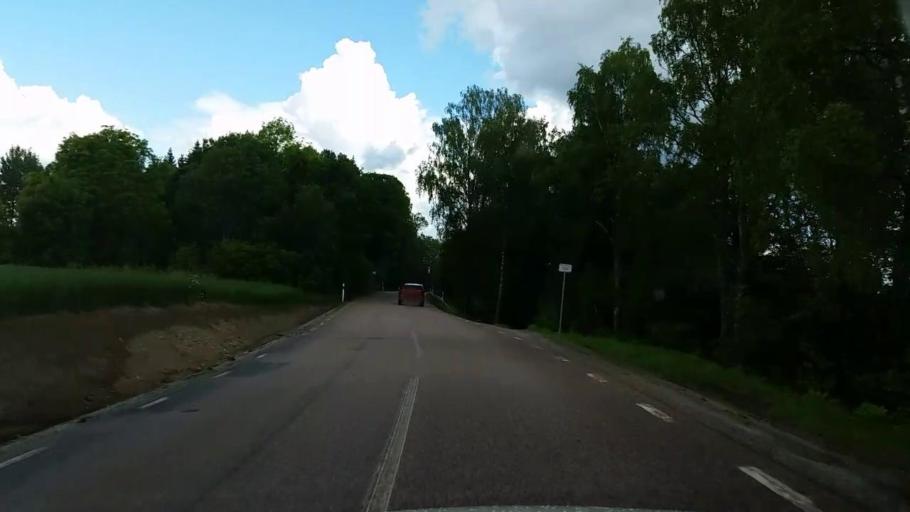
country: SE
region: Vaestmanland
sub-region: Skinnskattebergs Kommun
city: Skinnskatteberg
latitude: 59.8498
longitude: 15.8426
